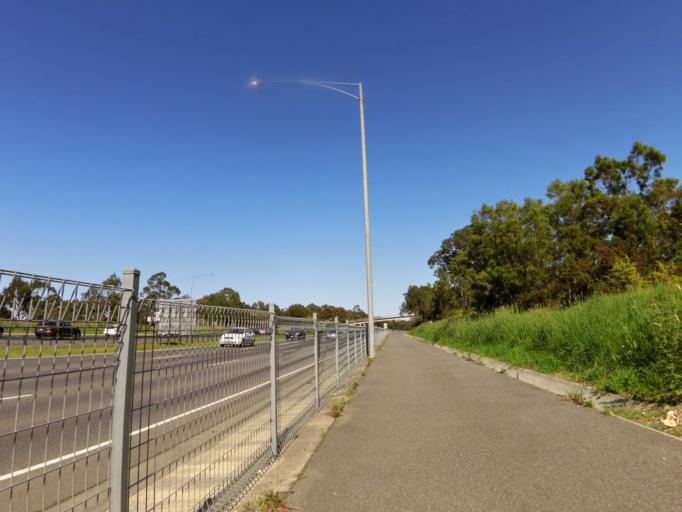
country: AU
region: Victoria
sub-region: Banyule
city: Greensborough
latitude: -37.6901
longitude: 145.1114
